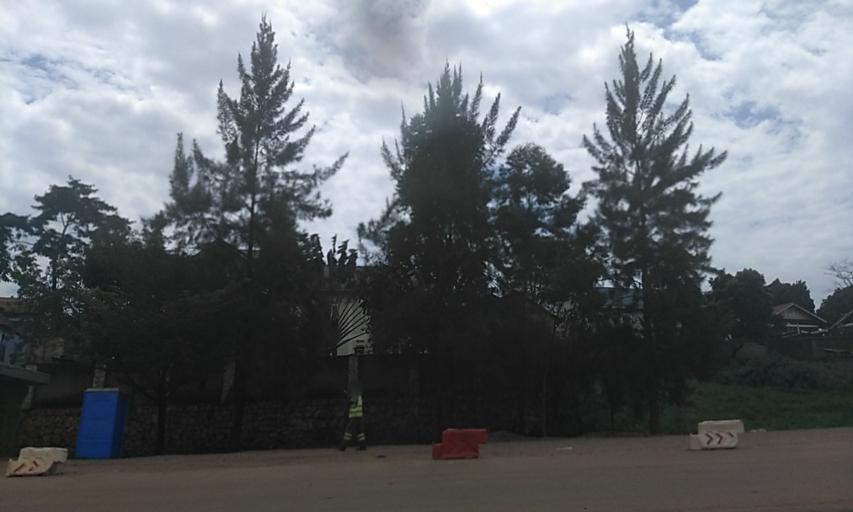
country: UG
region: Central Region
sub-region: Wakiso District
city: Kireka
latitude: 0.3657
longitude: 32.6106
